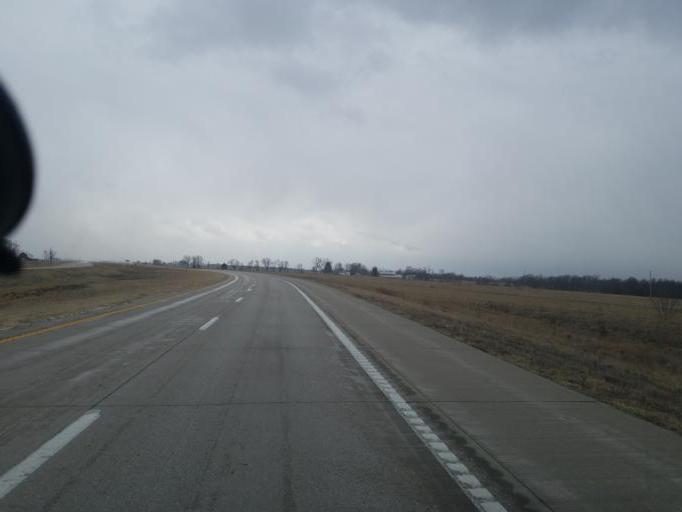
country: US
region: Missouri
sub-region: Randolph County
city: Huntsville
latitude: 39.5748
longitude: -92.4657
